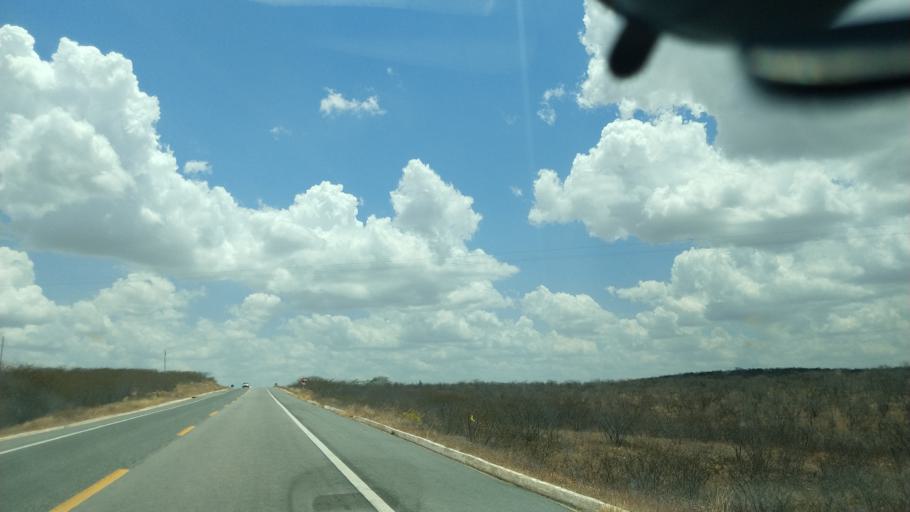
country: BR
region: Rio Grande do Norte
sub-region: Currais Novos
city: Currais Novos
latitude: -6.2477
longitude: -36.4709
